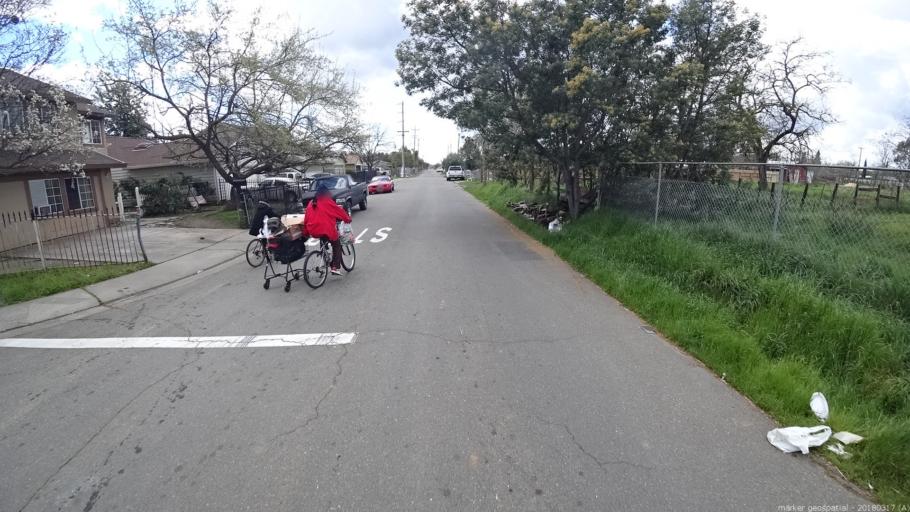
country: US
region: California
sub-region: Sacramento County
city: Florin
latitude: 38.4763
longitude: -121.4106
